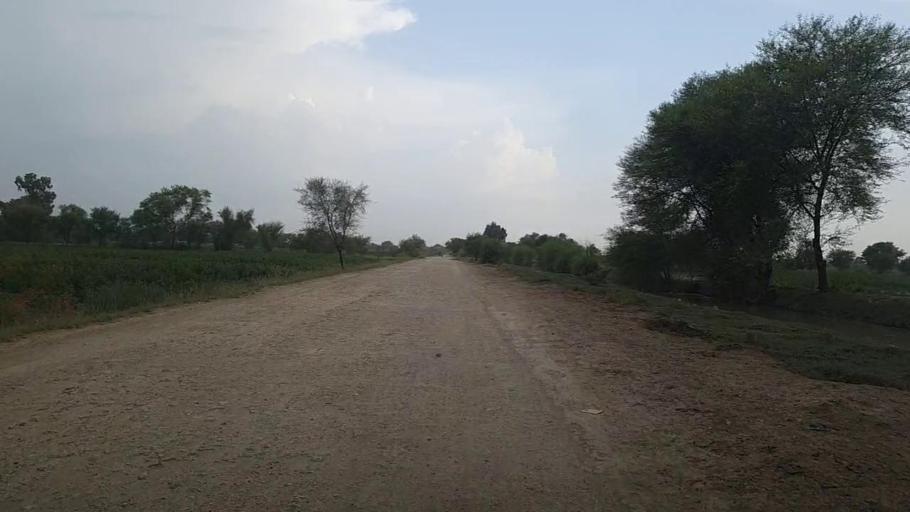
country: PK
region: Sindh
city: Khanpur
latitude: 27.8443
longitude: 69.4850
